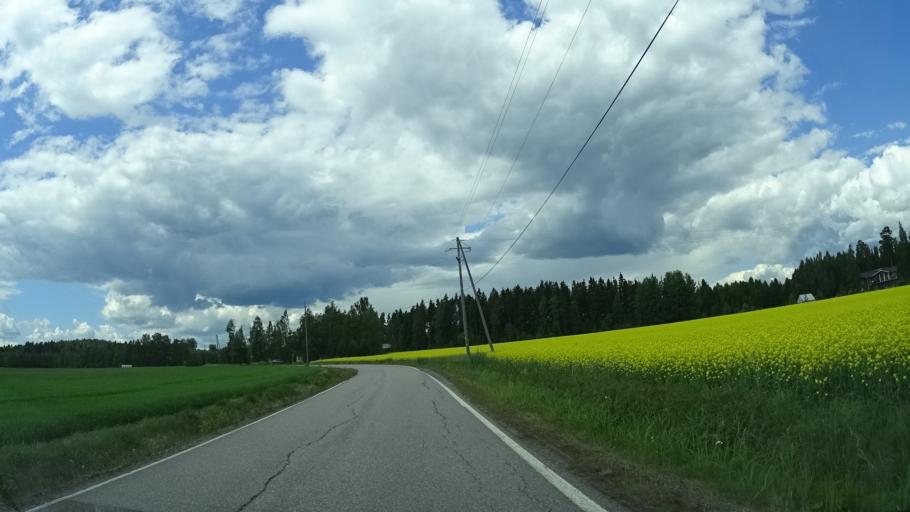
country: FI
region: Uusimaa
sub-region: Helsinki
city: Espoo
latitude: 60.4067
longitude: 24.6066
